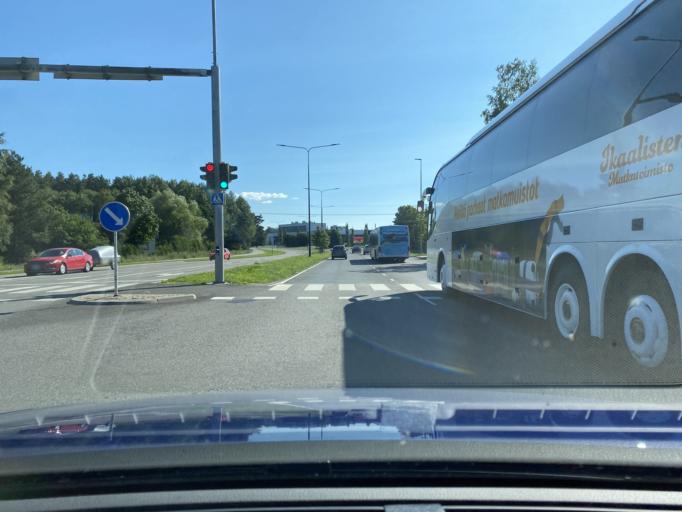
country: FI
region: Varsinais-Suomi
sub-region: Turku
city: Turku
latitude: 60.4753
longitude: 22.2662
